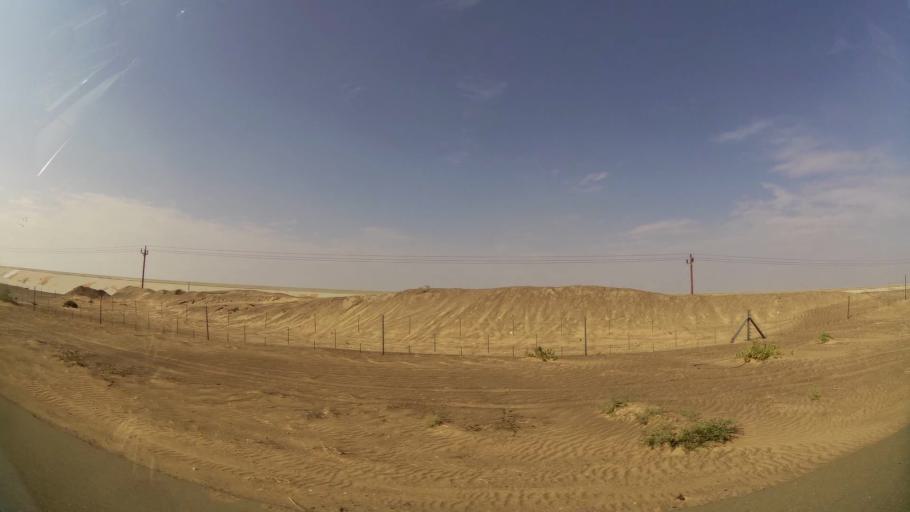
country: AE
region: Abu Dhabi
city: Al Ain
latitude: 24.0928
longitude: 55.8788
